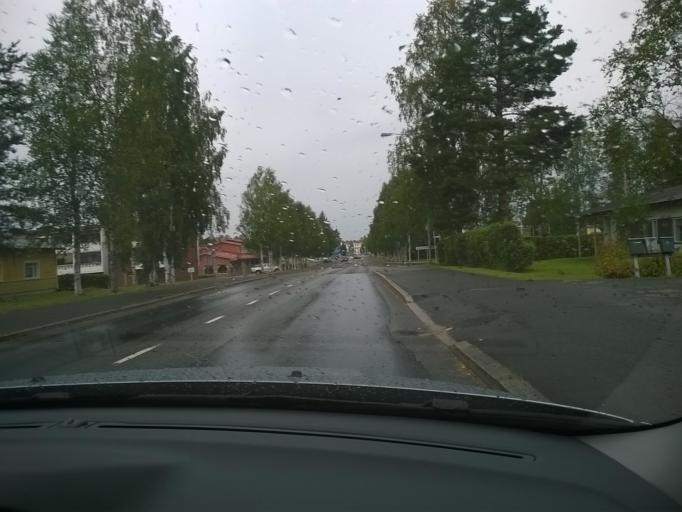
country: FI
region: Kainuu
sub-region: Kehys-Kainuu
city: Kuhmo
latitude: 64.1257
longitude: 29.5285
